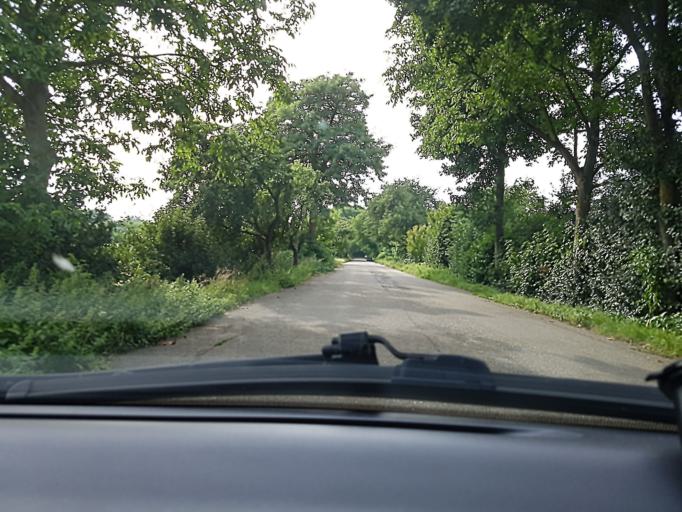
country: DE
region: Baden-Wuerttemberg
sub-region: Freiburg Region
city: Kehl
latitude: 48.5723
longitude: 7.8335
